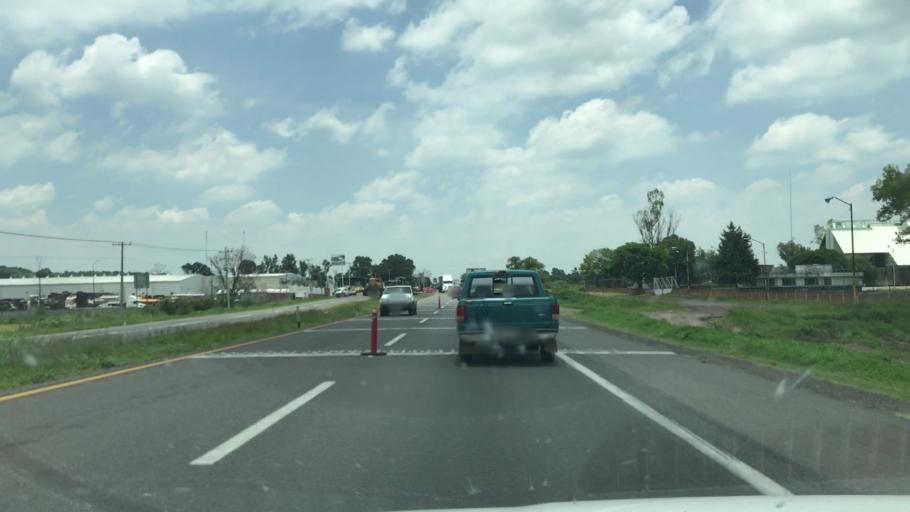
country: MX
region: Guanajuato
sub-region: Irapuato
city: San Ignacio de Rivera (Ojo de Agua)
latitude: 20.5300
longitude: -101.4604
